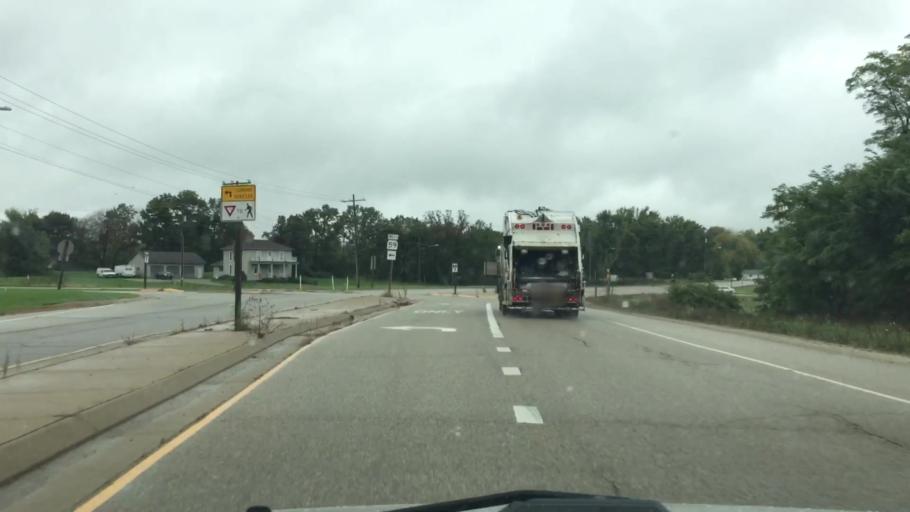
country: US
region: Wisconsin
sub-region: Walworth County
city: Whitewater
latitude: 42.8219
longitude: -88.7457
